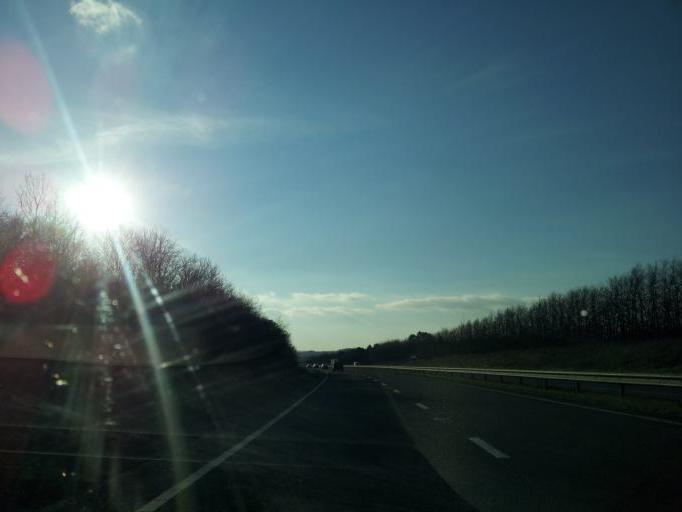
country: GB
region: England
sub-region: Devon
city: Okehampton
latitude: 50.7400
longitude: -3.9619
